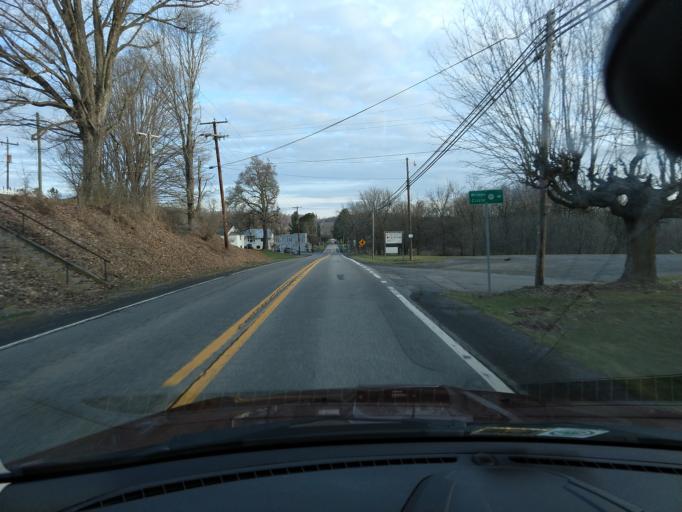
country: US
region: West Virginia
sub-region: Greenbrier County
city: Lewisburg
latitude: 37.9237
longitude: -80.3844
